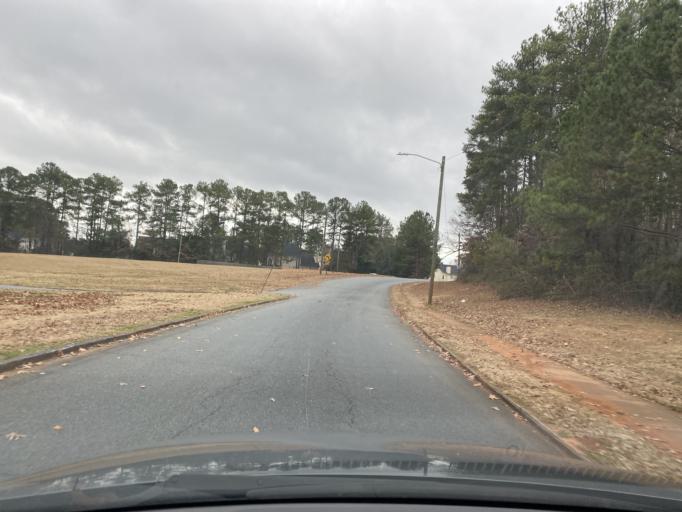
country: US
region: Georgia
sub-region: DeKalb County
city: Redan
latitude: 33.7011
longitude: -84.1652
